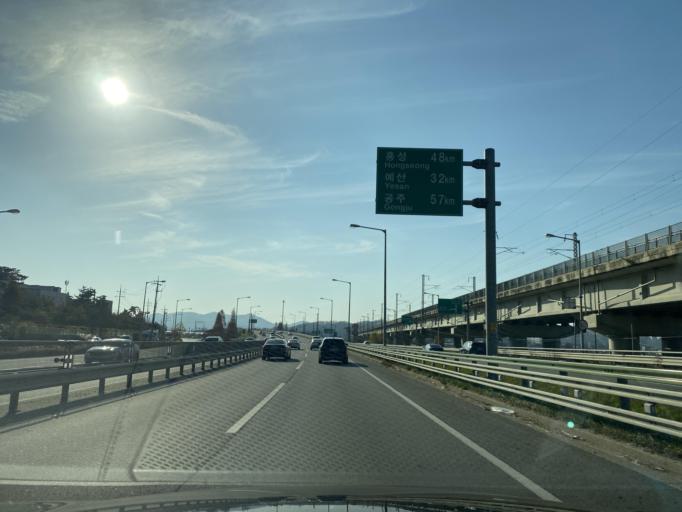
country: KR
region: Chungcheongnam-do
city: Asan
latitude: 36.7750
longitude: 127.0468
